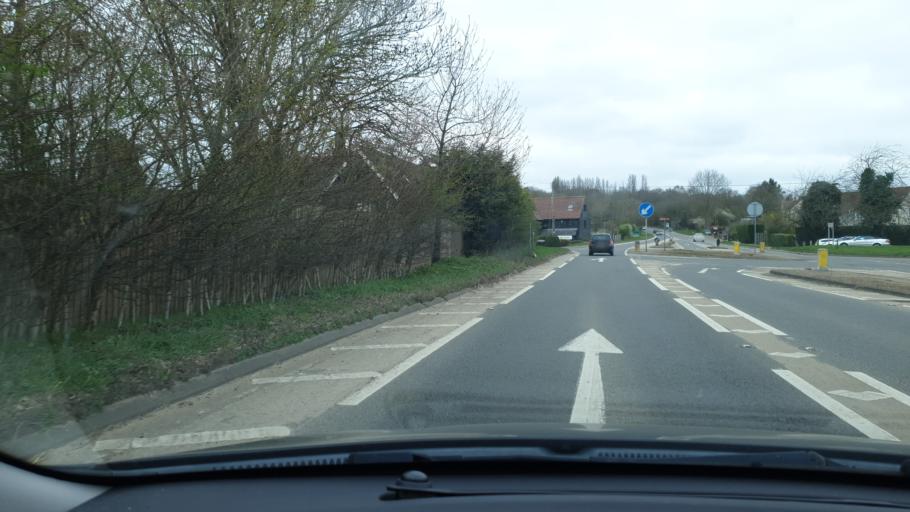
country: GB
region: England
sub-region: Essex
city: Great Horkesley
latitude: 51.9710
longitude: 0.8639
